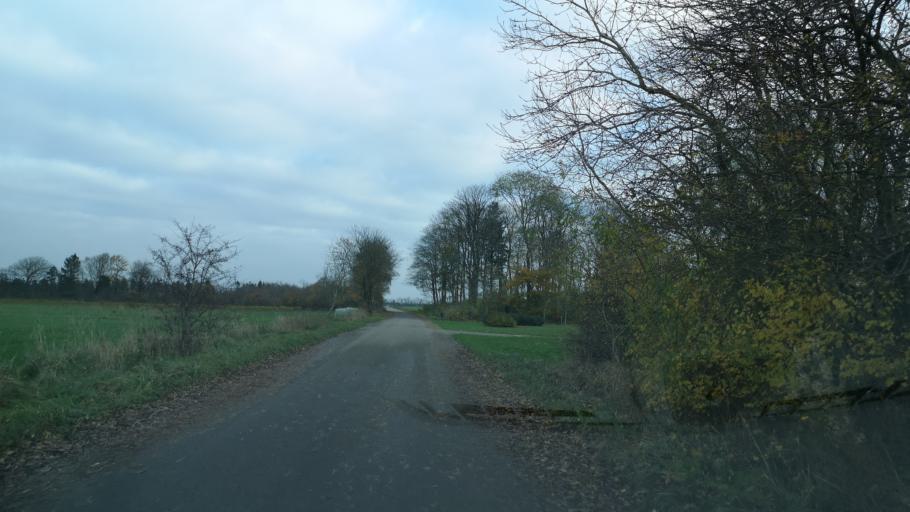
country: DK
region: Central Jutland
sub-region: Ringkobing-Skjern Kommune
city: Videbaek
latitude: 56.0324
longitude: 8.6023
